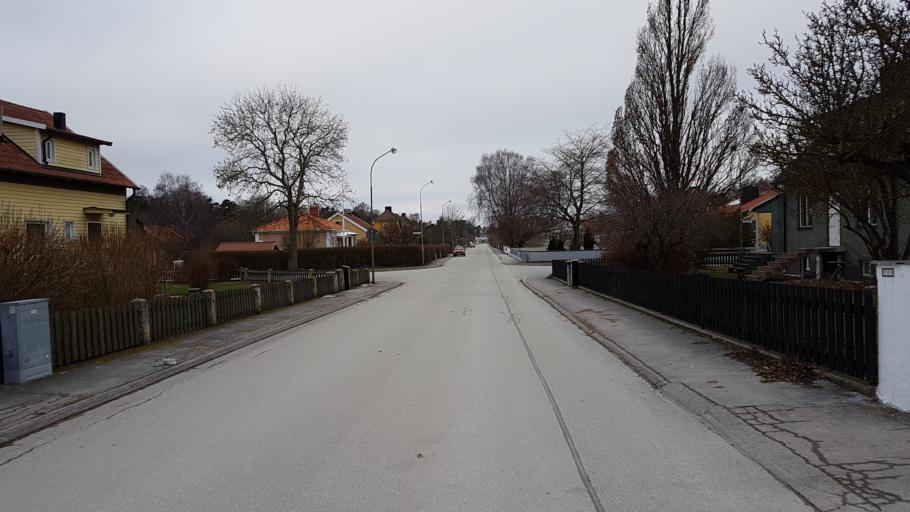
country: SE
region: Gotland
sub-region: Gotland
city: Visby
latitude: 57.6221
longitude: 18.3073
